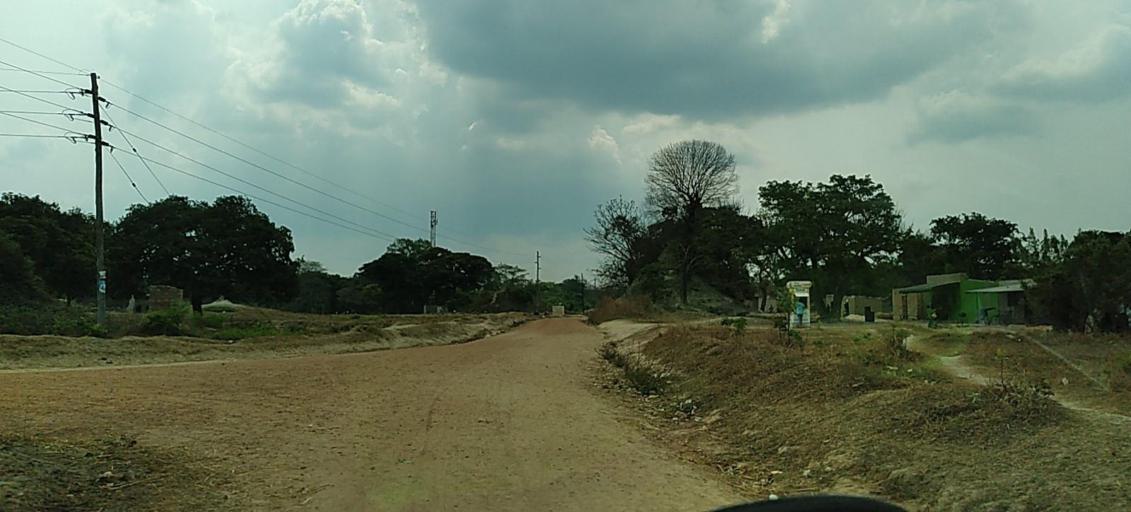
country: ZM
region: North-Western
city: Solwezi
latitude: -12.7866
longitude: 26.5168
